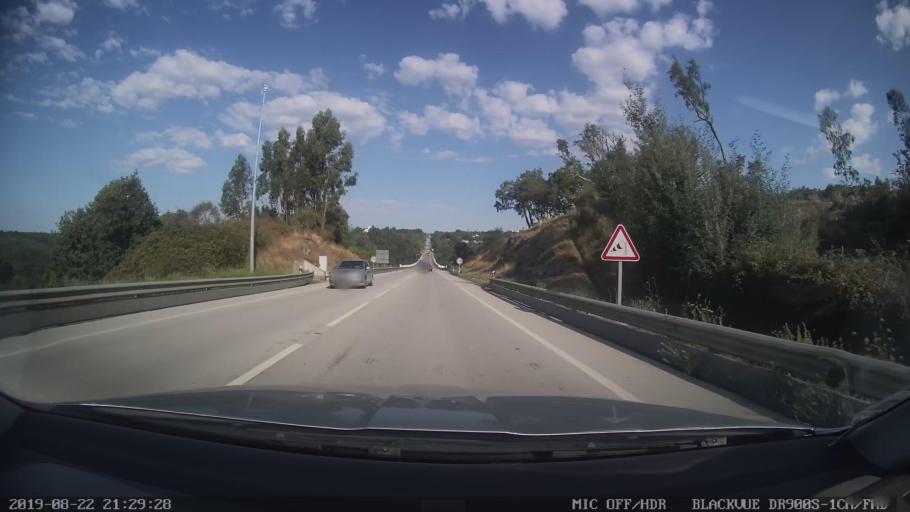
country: PT
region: Leiria
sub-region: Pedrogao Grande
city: Pedrogao Grande
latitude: 39.9026
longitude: -8.1358
